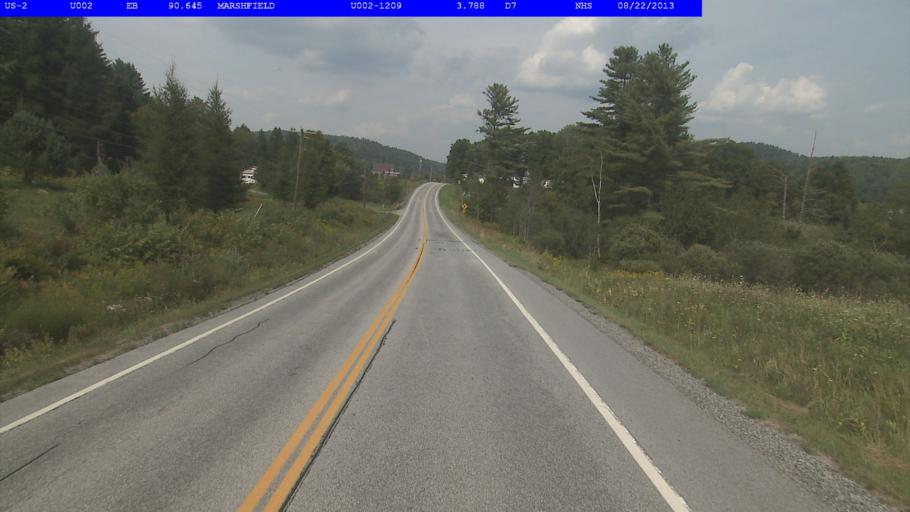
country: US
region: Vermont
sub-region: Washington County
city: Barre
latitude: 44.3204
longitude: -72.3827
